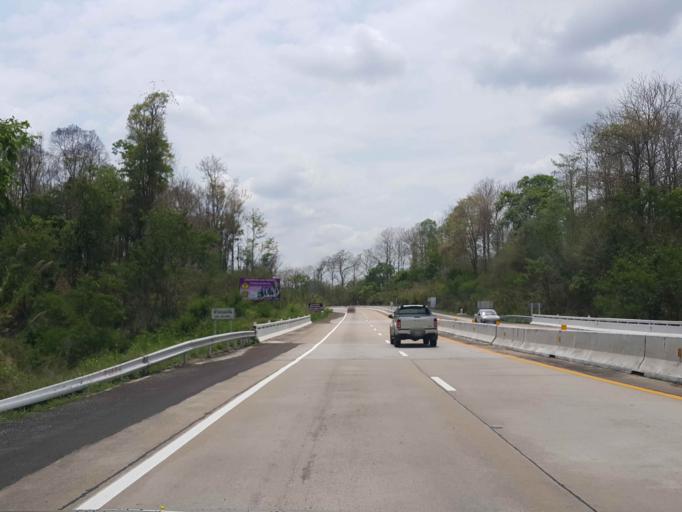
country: TH
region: Lampang
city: Hang Chat
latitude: 18.3636
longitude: 99.2378
